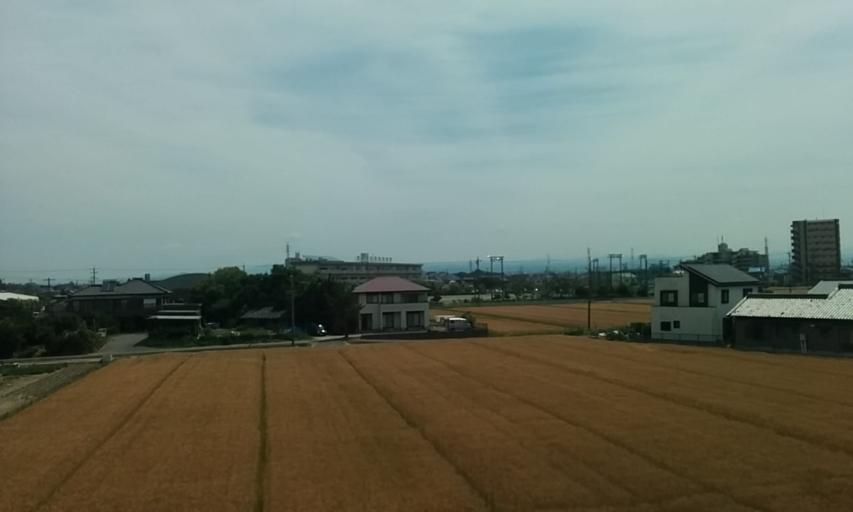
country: JP
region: Aichi
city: Anjo
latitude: 34.9417
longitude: 137.0856
